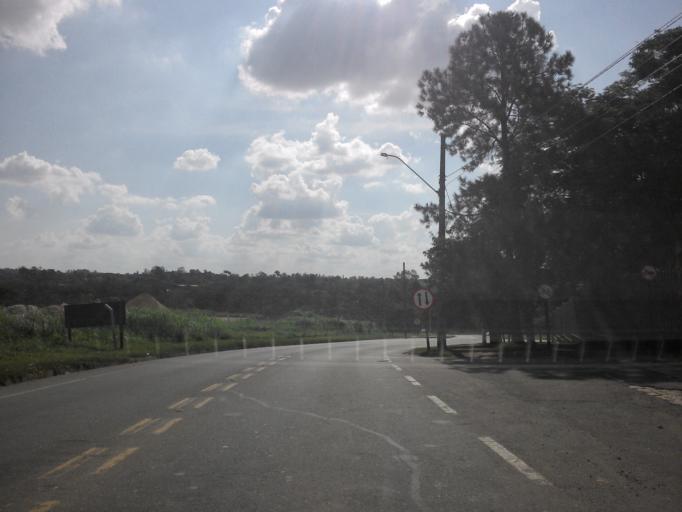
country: BR
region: Sao Paulo
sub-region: Valinhos
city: Valinhos
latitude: -22.9964
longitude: -47.0055
